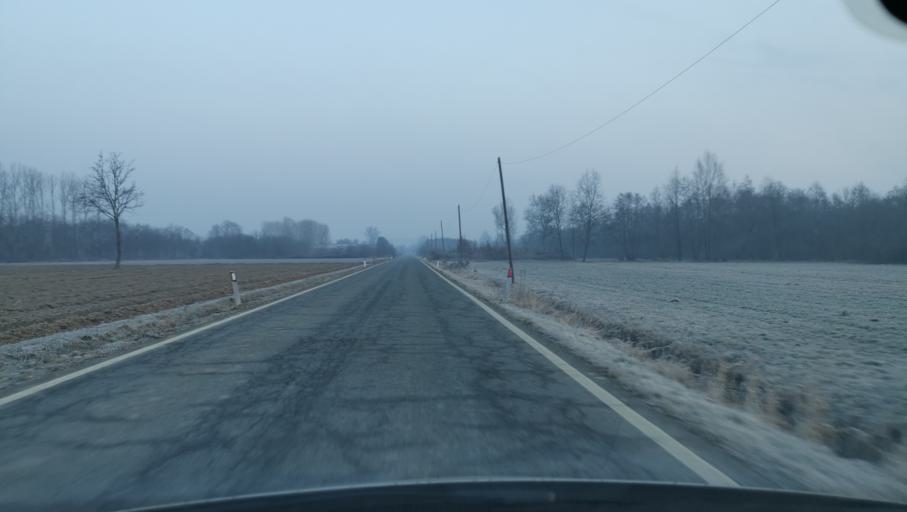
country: IT
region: Piedmont
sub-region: Provincia di Torino
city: San Giusto Canavese
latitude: 45.2947
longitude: 7.8122
